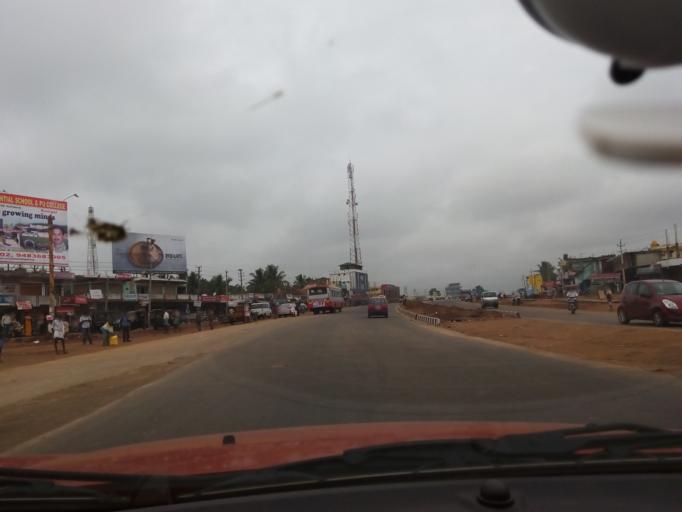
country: IN
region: Karnataka
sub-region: Hassan
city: Shravanabelagola
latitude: 12.9519
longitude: 76.5745
